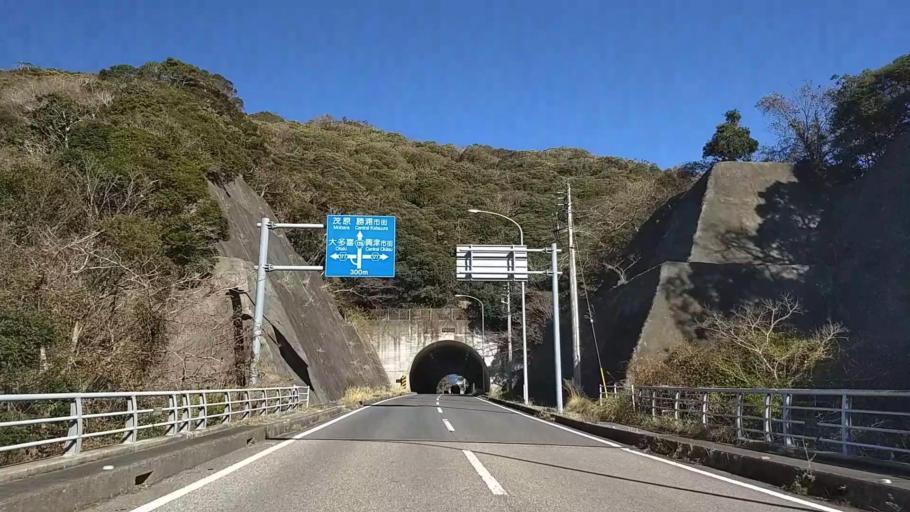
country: JP
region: Chiba
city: Katsuura
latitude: 35.1357
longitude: 140.2425
